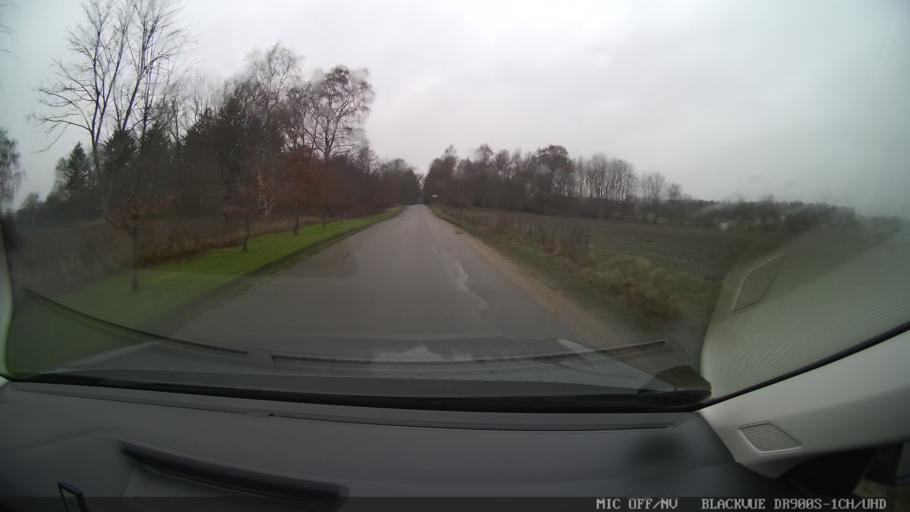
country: DK
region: Central Jutland
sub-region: Viborg Kommune
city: Karup
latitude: 56.2902
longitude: 9.1628
